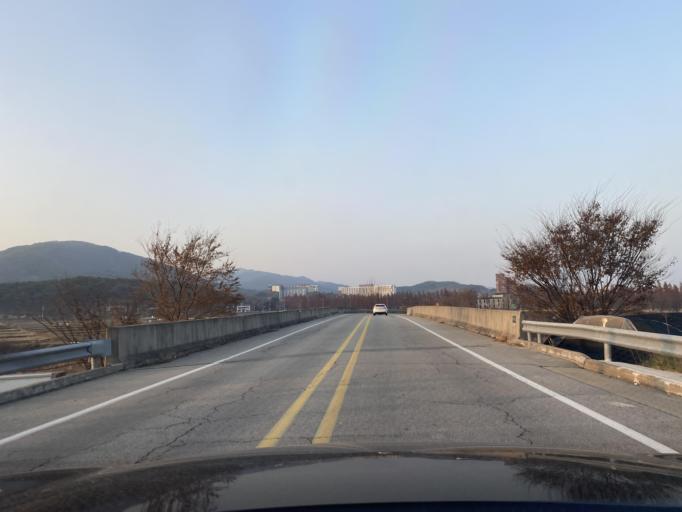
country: KR
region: Chungcheongnam-do
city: Hongsung
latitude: 36.6841
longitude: 126.6589
